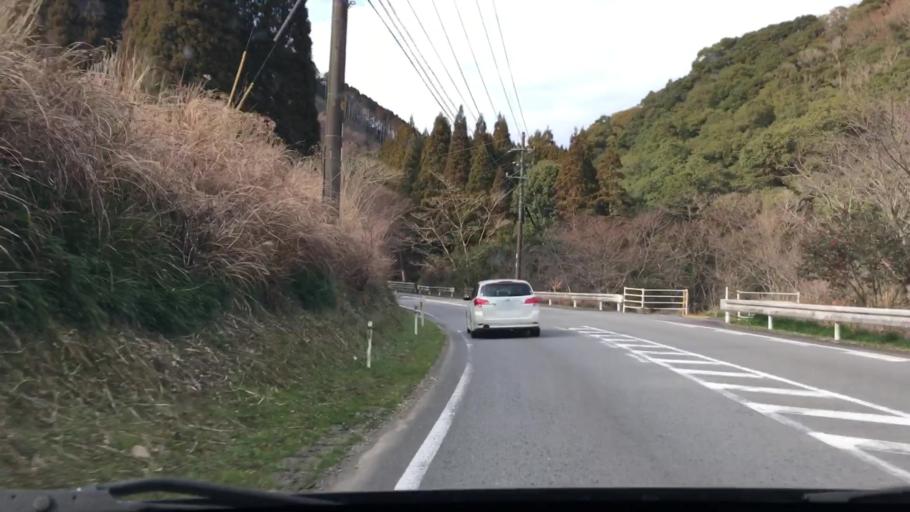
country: JP
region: Miyazaki
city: Nichinan
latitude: 31.7463
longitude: 131.3354
